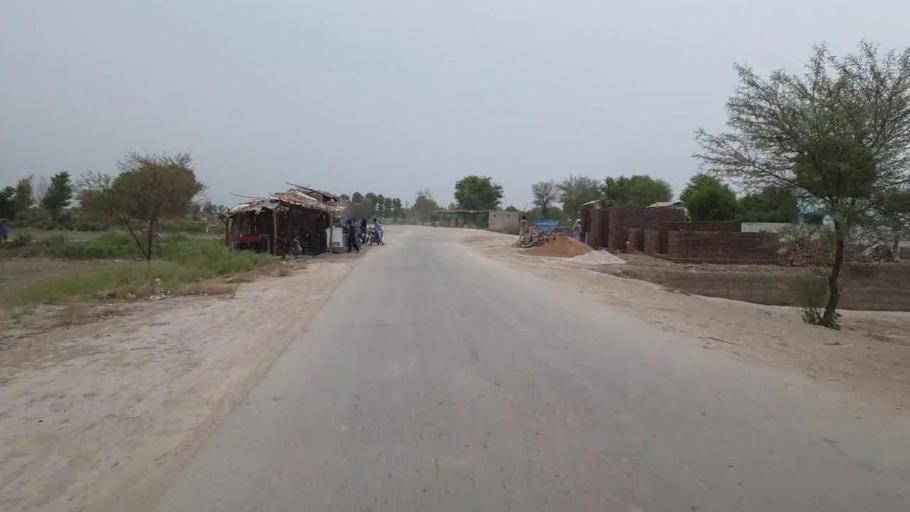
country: PK
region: Sindh
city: Bandhi
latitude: 26.5452
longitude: 68.2194
